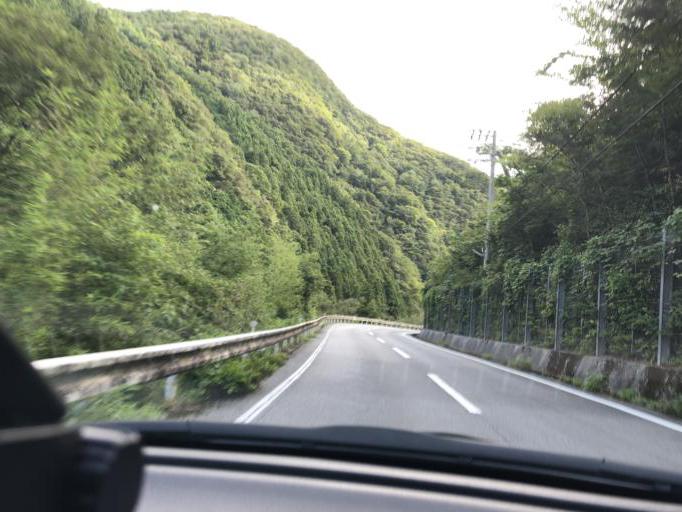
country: JP
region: Kochi
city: Kochi-shi
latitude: 33.6331
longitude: 133.5193
